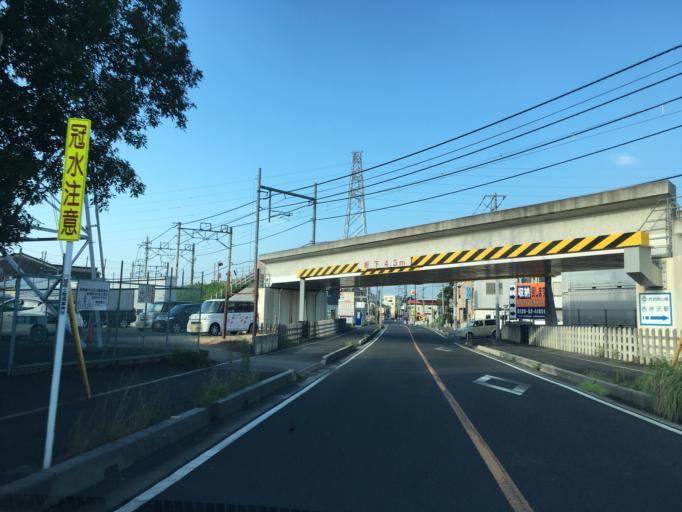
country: JP
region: Saitama
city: Tokorozawa
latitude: 35.7840
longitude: 139.4472
